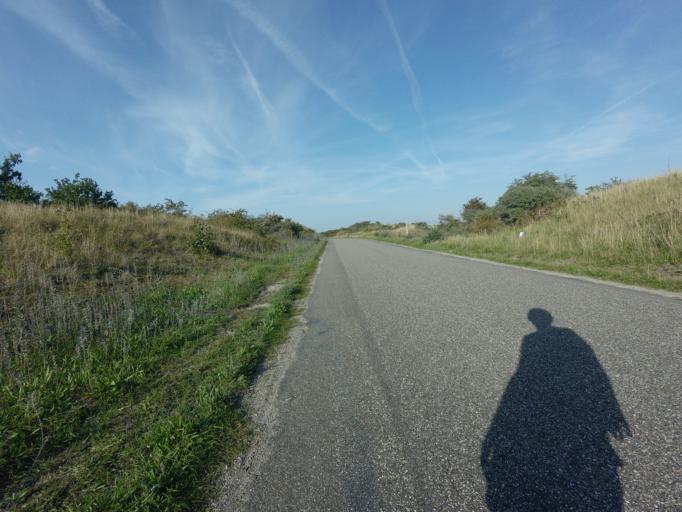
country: NL
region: Friesland
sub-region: Gemeente Schiermonnikoog
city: Schiermonnikoog
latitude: 53.4893
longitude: 6.1822
